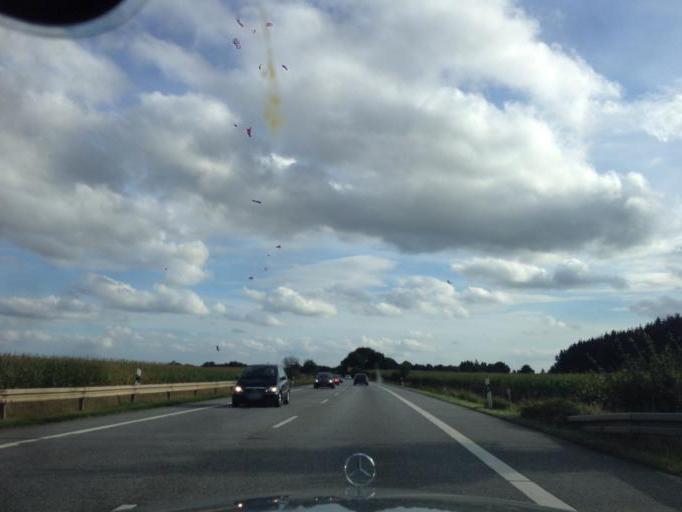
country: DE
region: Schleswig-Holstein
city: Rickling
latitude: 53.9933
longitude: 10.1837
